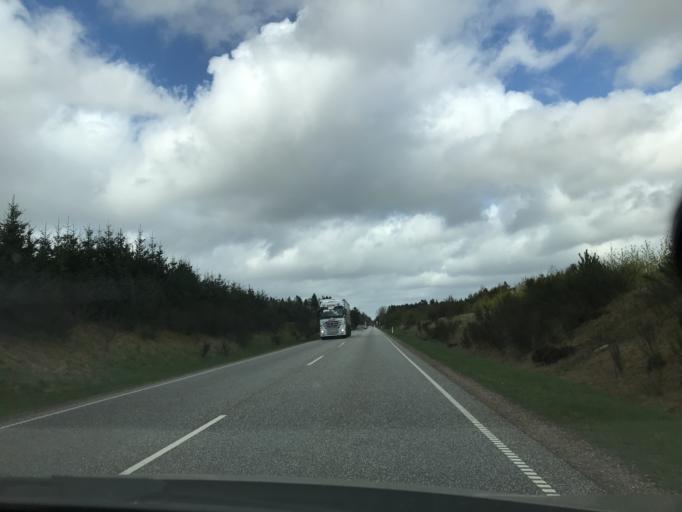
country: DK
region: Central Jutland
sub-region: Herning Kommune
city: Sunds
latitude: 56.3782
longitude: 8.9870
